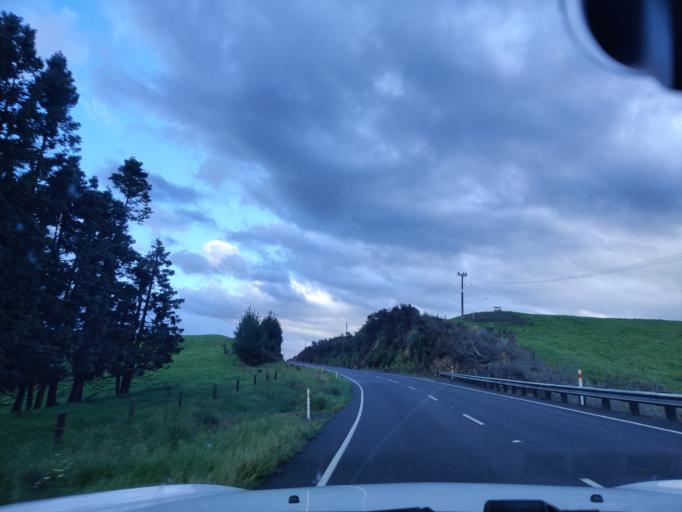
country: NZ
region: Waikato
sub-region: South Waikato District
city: Tokoroa
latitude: -38.3749
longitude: 175.7927
